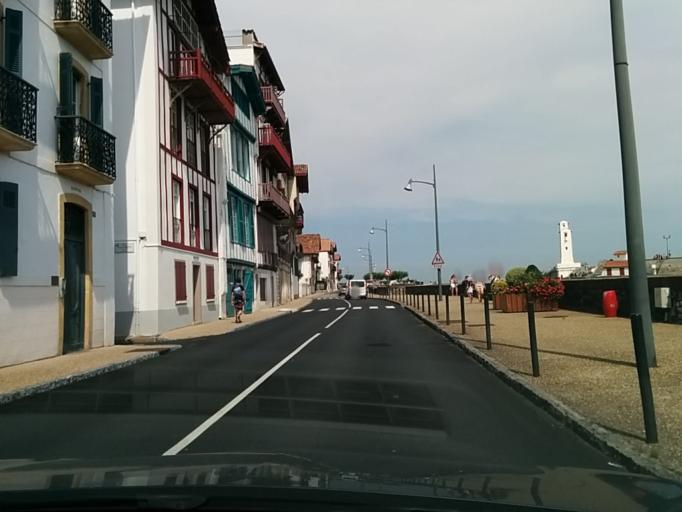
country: FR
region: Aquitaine
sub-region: Departement des Pyrenees-Atlantiques
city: Saint-Jean-de-Luz
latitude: 43.3860
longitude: -1.6680
